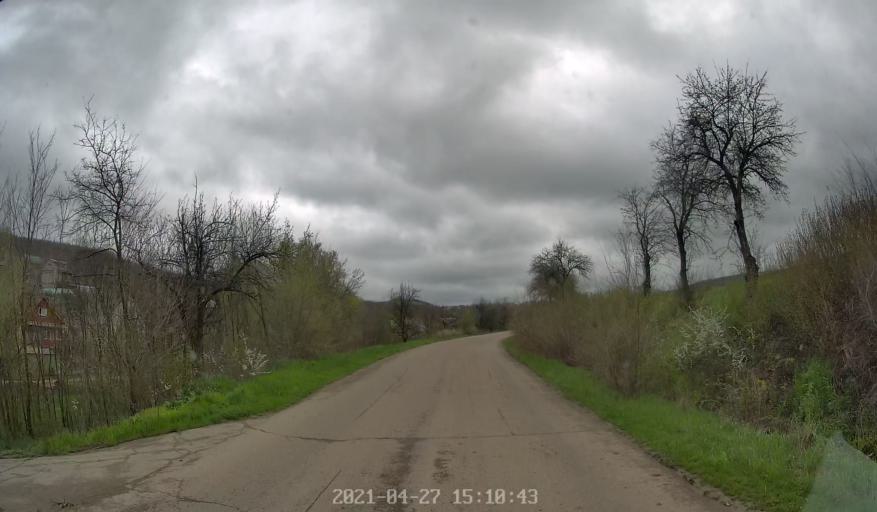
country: MD
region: Chisinau
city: Vadul lui Voda
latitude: 47.0377
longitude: 29.0322
